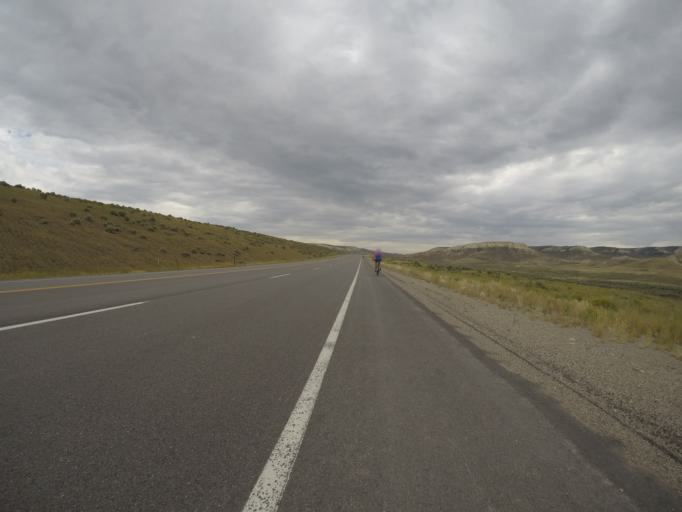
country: US
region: Wyoming
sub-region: Lincoln County
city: Kemmerer
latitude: 41.8104
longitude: -110.6825
